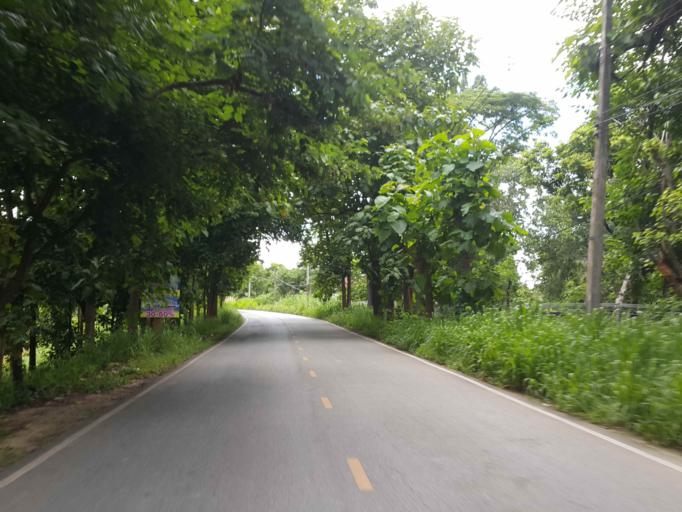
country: TH
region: Chiang Mai
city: San Sai
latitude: 18.9109
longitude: 98.9420
